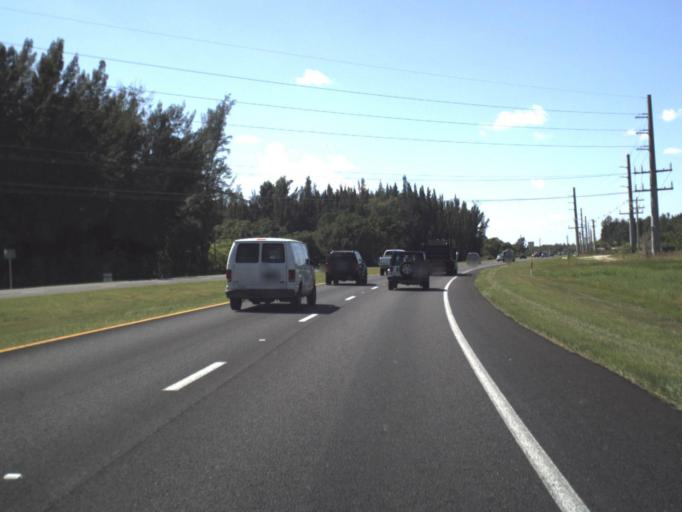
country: US
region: Florida
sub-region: Lee County
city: Cape Coral
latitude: 26.6381
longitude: -82.0098
